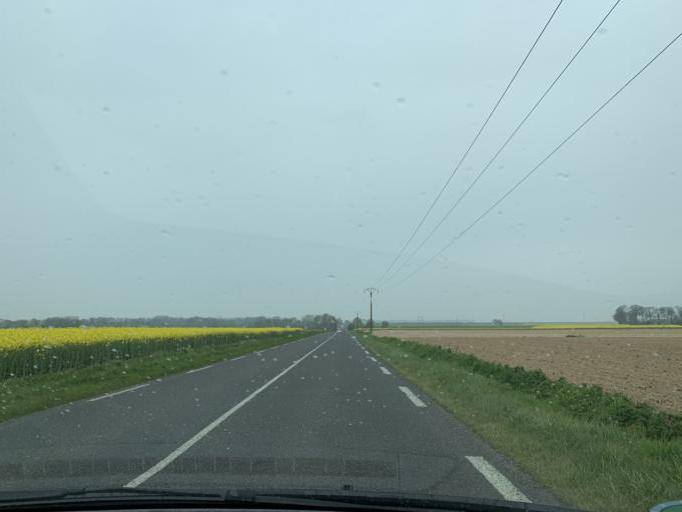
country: FR
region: Haute-Normandie
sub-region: Departement de la Seine-Maritime
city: Cany-Barville
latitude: 49.7967
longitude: 0.6640
